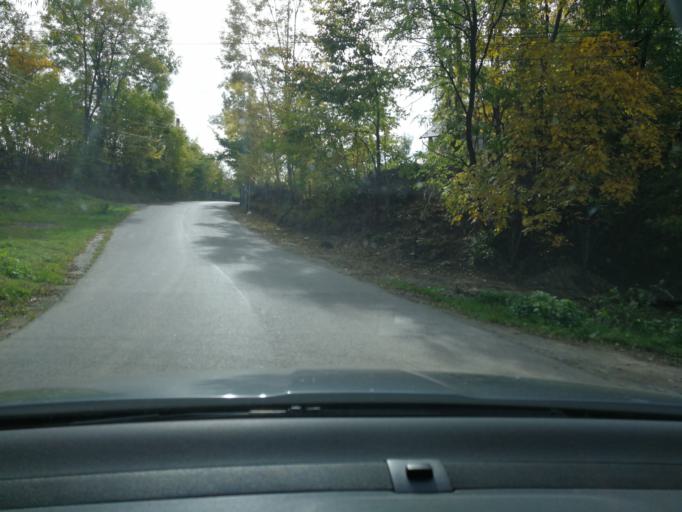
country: RO
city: Brebu Manastirei
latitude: 45.1912
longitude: 25.7659
